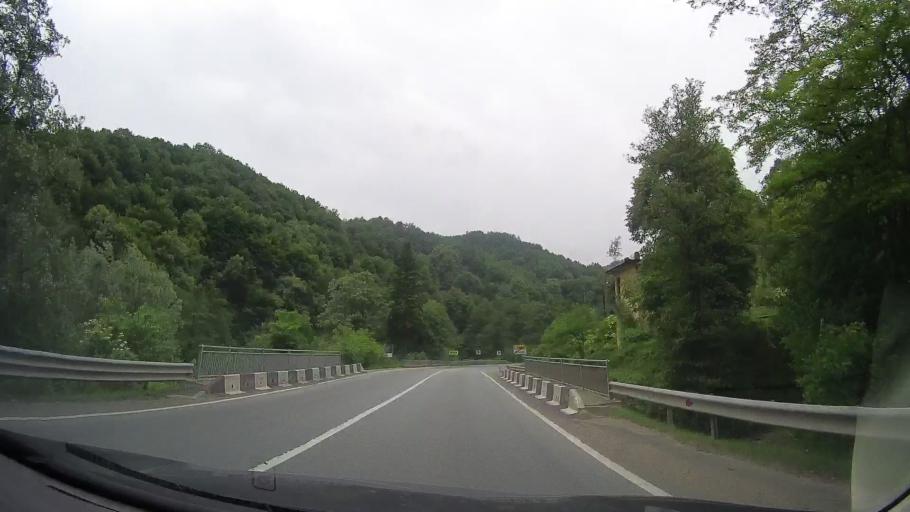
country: RO
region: Caras-Severin
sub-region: Comuna Armenis
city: Armenis
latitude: 45.1953
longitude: 22.3098
